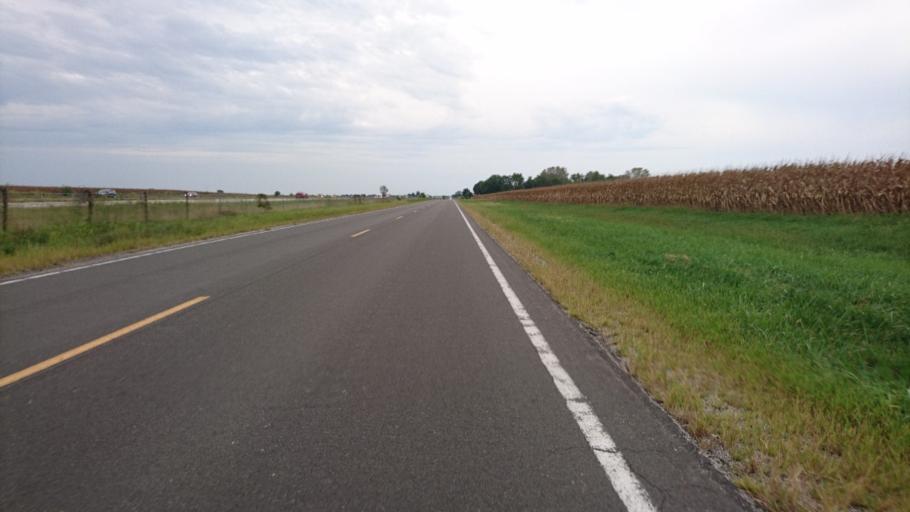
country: US
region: Illinois
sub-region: Sangamon County
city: Chatham
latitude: 39.6628
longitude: -89.6481
